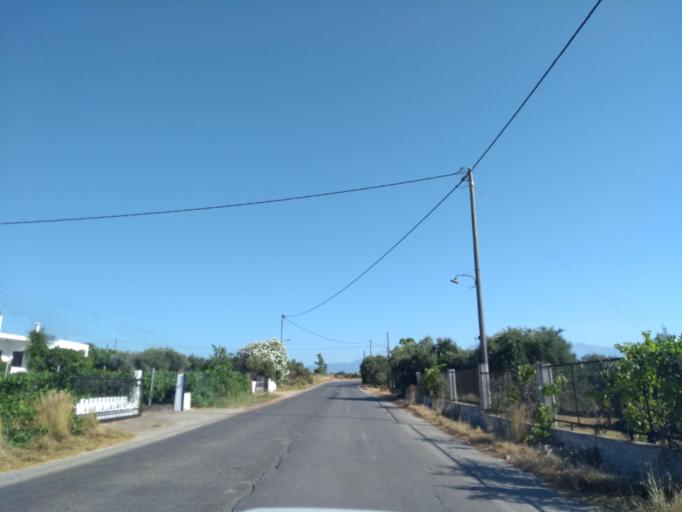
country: GR
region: Crete
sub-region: Nomos Chanias
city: Pithari
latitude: 35.5792
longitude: 24.0937
